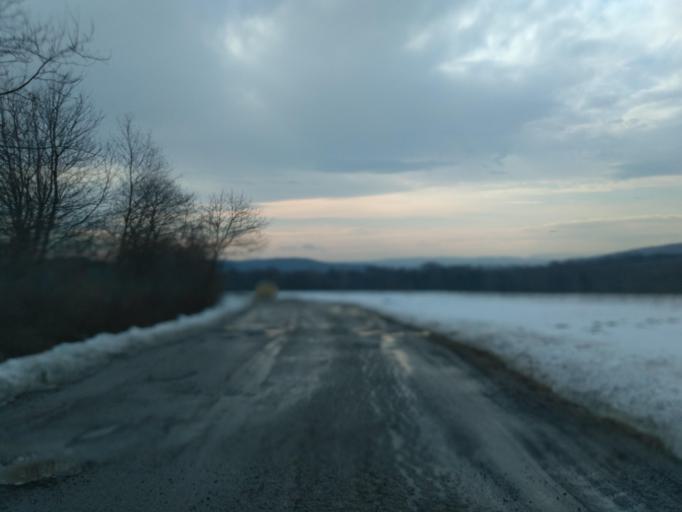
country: PL
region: Subcarpathian Voivodeship
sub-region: Powiat brzozowski
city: Dydnia
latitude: 49.6463
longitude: 22.1598
